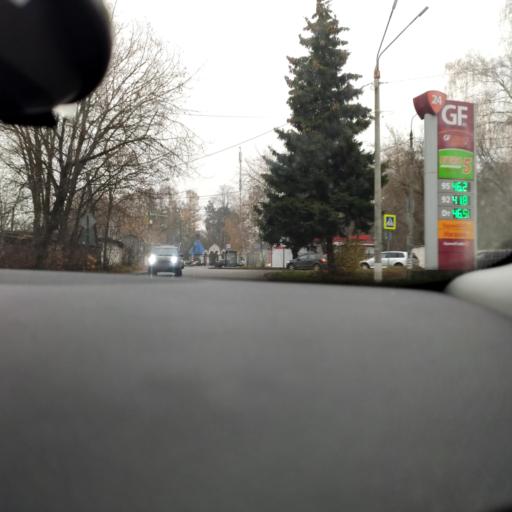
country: RU
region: Moskovskaya
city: Nakhabino
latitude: 55.8425
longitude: 37.1571
